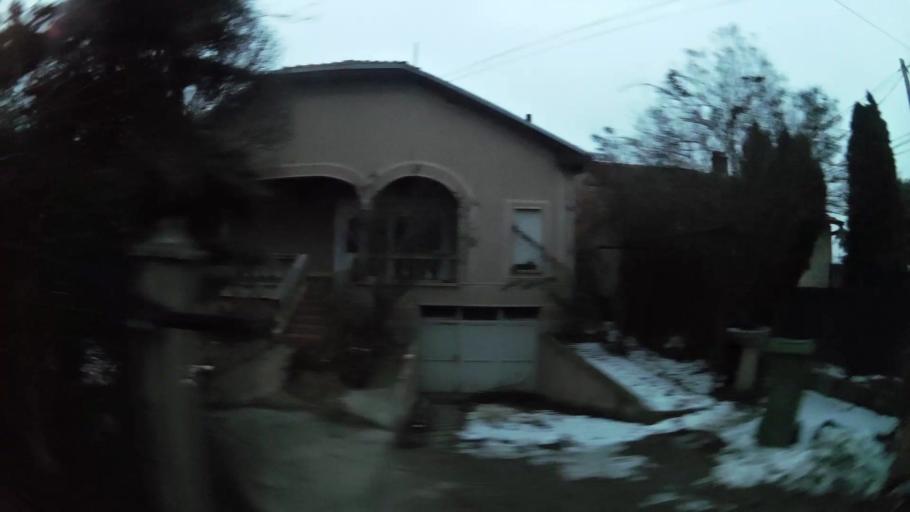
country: MK
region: Kisela Voda
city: Kisela Voda
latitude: 41.9751
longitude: 21.4941
